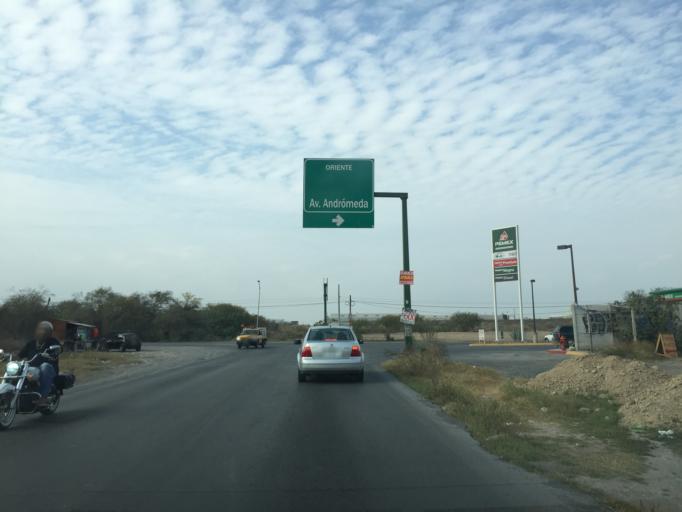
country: MX
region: Nuevo Leon
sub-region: Apodaca
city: Fraccionamiento Cosmopolis Octavo Sector
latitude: 25.8110
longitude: -100.2502
